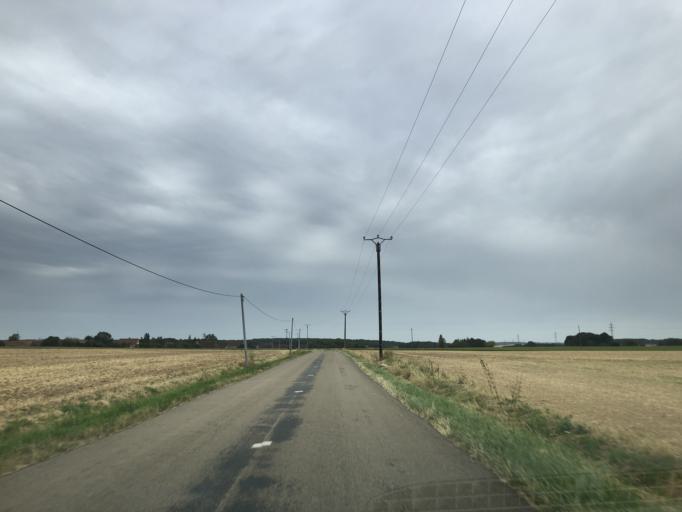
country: FR
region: Centre
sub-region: Departement du Loiret
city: Douchy
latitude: 47.9797
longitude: 3.1423
